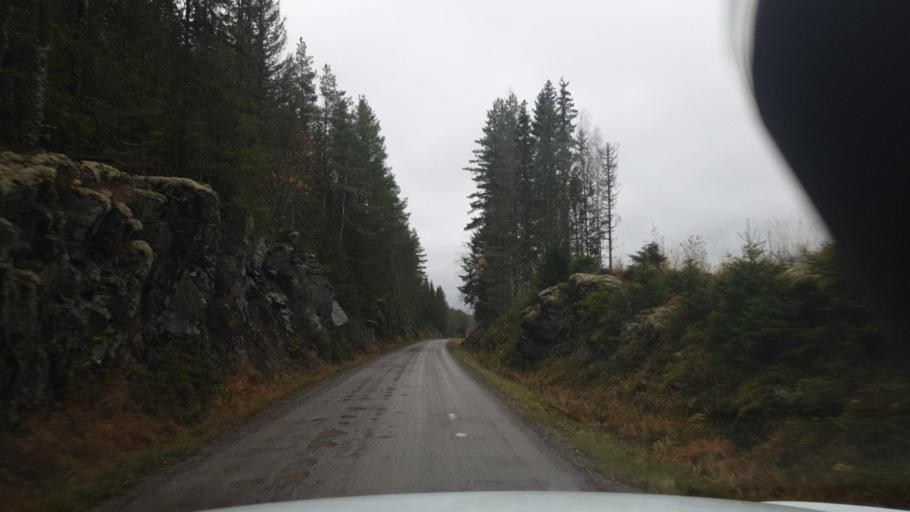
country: SE
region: Vaermland
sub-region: Eda Kommun
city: Charlottenberg
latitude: 60.0201
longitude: 12.5066
